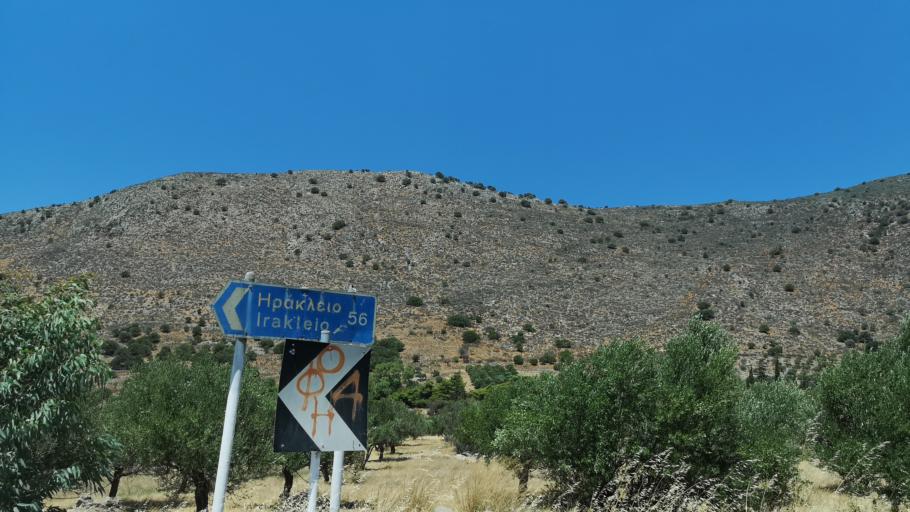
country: GR
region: Crete
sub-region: Nomos Lasithiou
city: Neapoli
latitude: 35.2455
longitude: 25.6406
